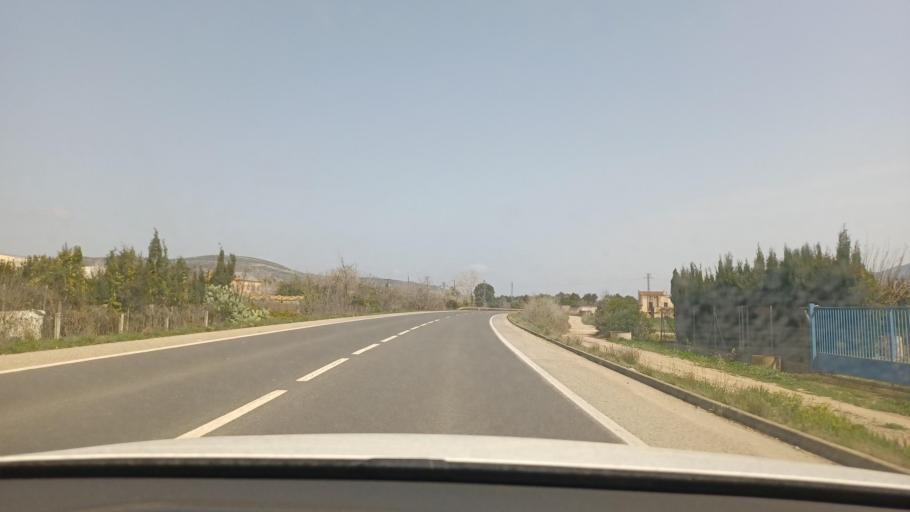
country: ES
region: Catalonia
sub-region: Provincia de Tarragona
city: Ulldecona
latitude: 40.5952
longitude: 0.4505
